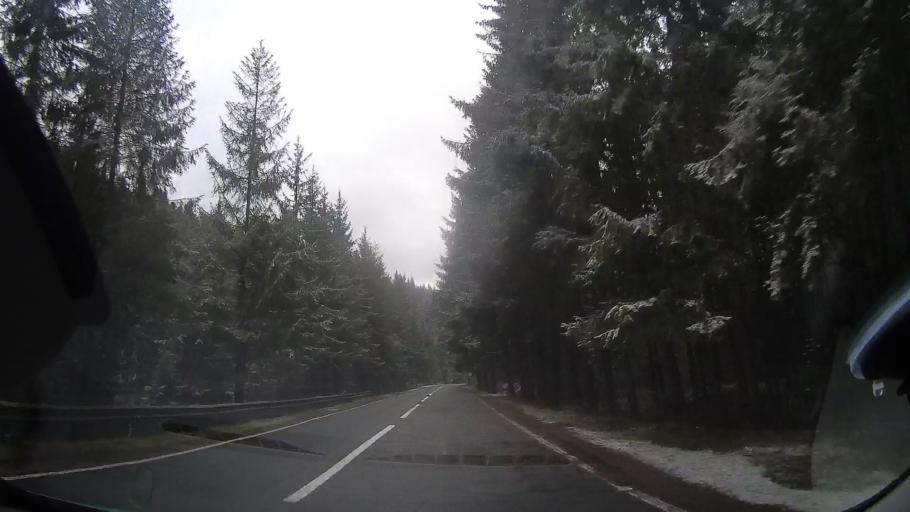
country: RO
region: Cluj
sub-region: Comuna Calatele
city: Calatele
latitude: 46.7393
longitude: 23.0179
